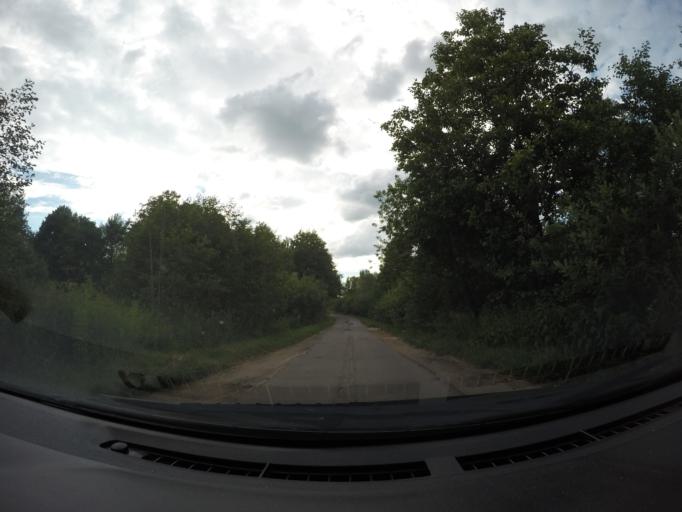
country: RU
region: Moskovskaya
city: Rechitsy
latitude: 55.6069
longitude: 38.5124
